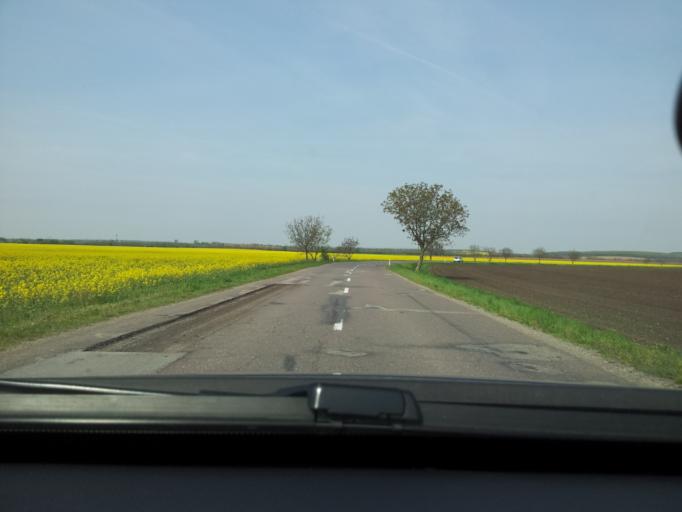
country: SK
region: Nitriansky
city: Tlmace
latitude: 48.2158
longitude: 18.5080
